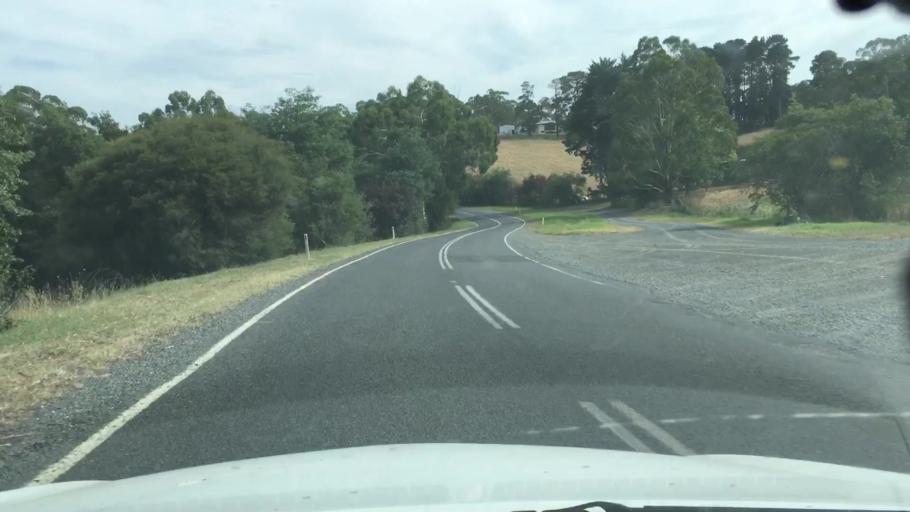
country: AU
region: Victoria
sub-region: Yarra Ranges
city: Woori Yallock
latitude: -37.7928
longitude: 145.5215
